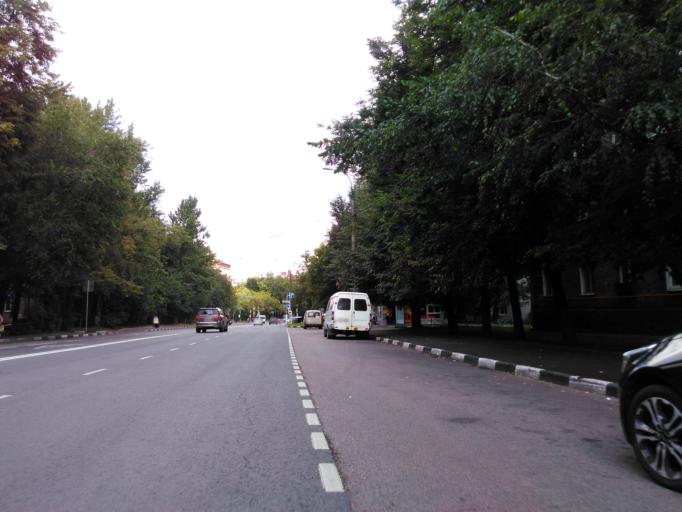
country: RU
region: Moscow
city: Kotlovka
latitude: 55.6757
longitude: 37.5984
